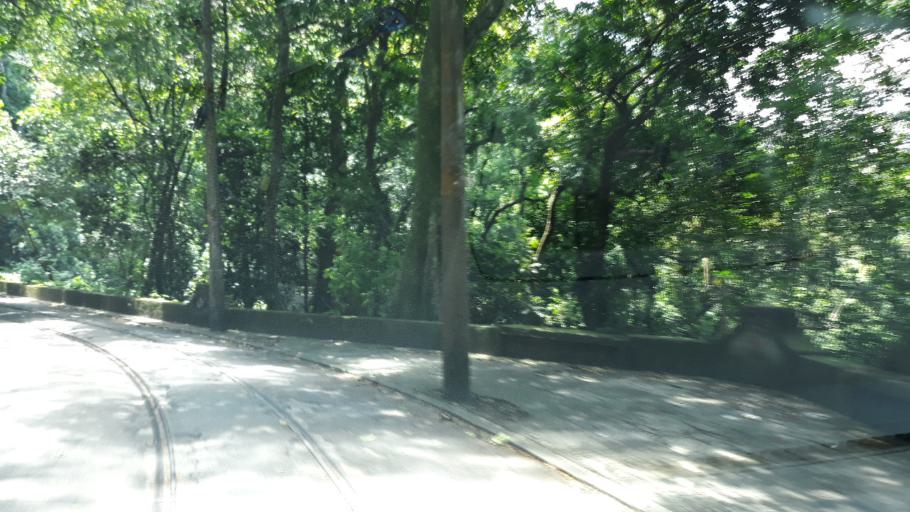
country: BR
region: Rio de Janeiro
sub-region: Rio De Janeiro
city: Rio de Janeiro
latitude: -22.9416
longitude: -43.2101
